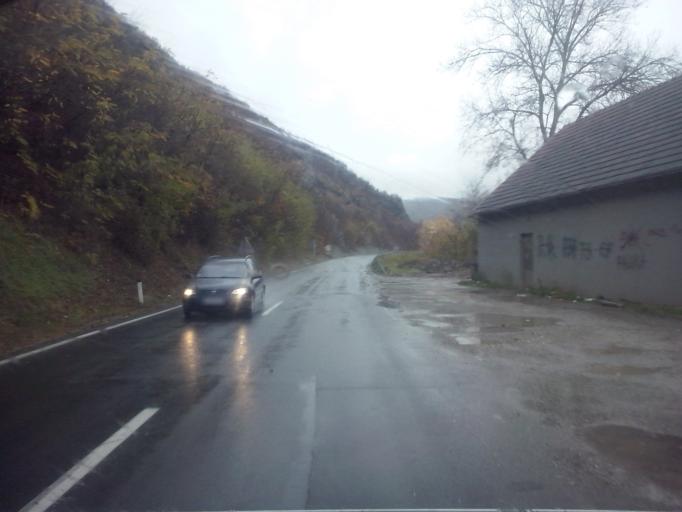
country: RS
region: Central Serbia
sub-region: Raski Okrug
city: Raska
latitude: 43.3542
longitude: 20.6396
